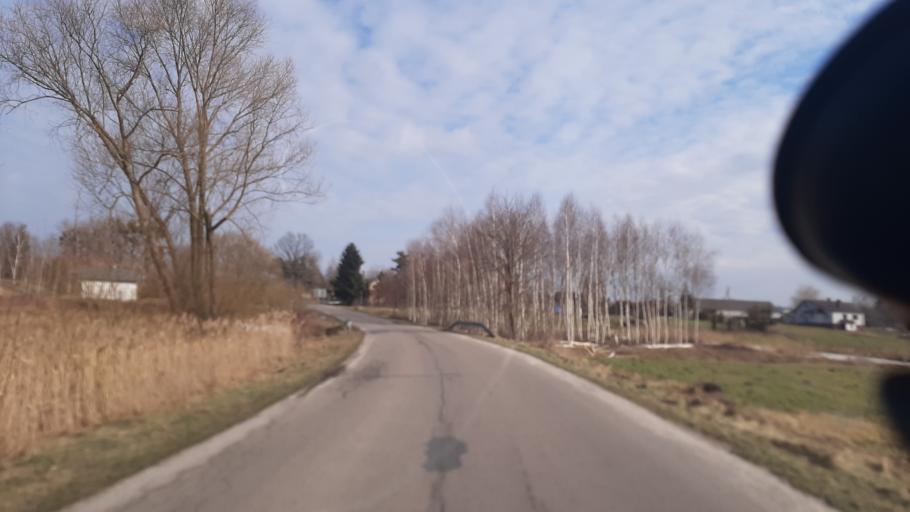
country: PL
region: Lublin Voivodeship
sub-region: Powiat lubartowski
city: Uscimow Stary
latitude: 51.4694
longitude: 22.9559
